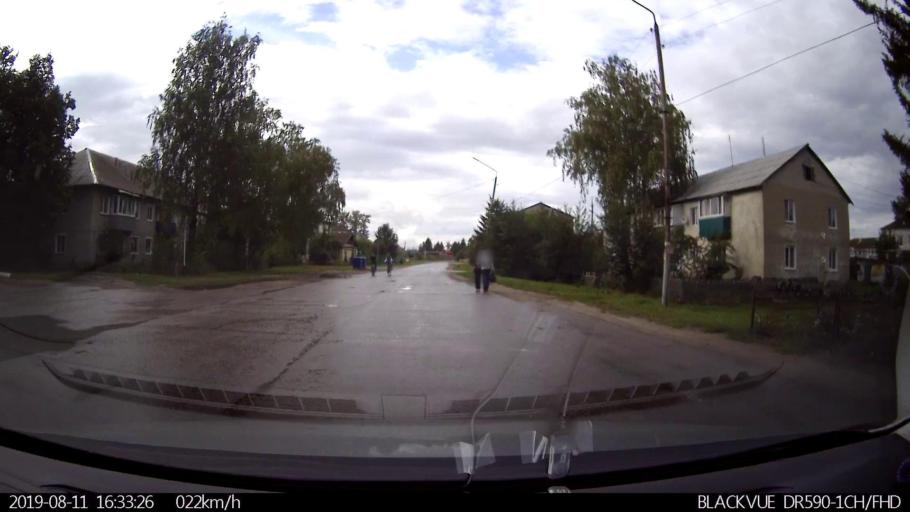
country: RU
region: Ulyanovsk
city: Mayna
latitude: 54.1147
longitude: 47.6256
